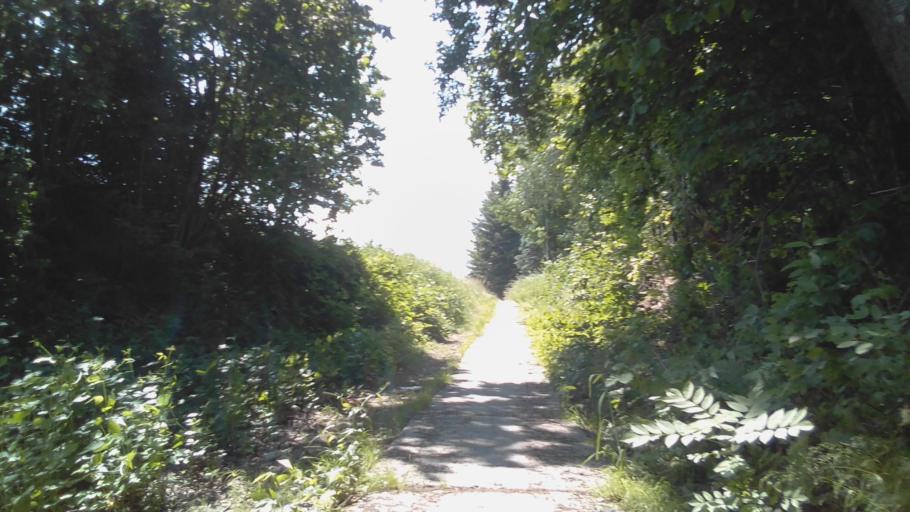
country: PL
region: Subcarpathian Voivodeship
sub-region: Powiat strzyzowski
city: Strzyzow
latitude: 49.8577
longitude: 21.7821
